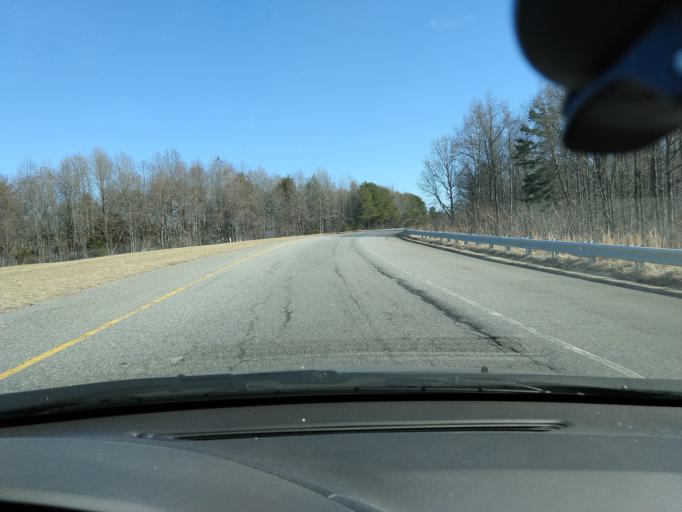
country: US
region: North Carolina
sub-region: Guilford County
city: Oak Ridge
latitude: 36.1075
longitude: -79.9639
